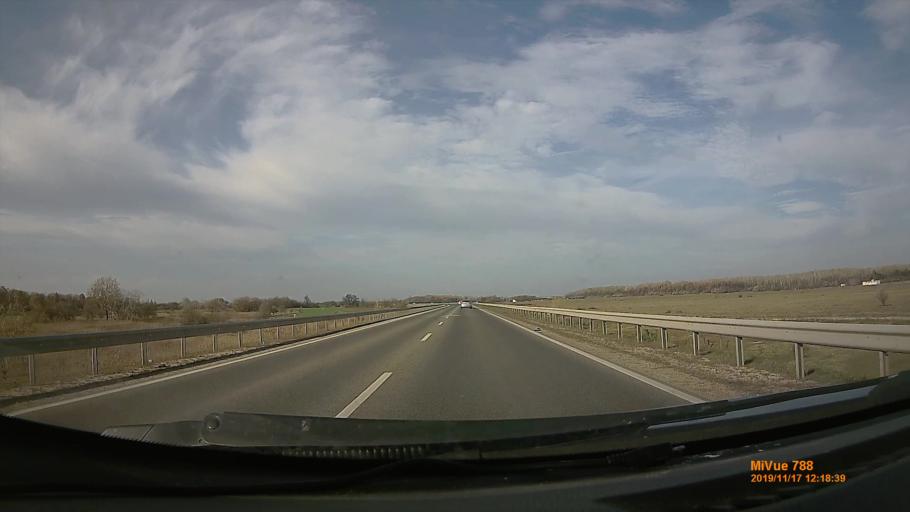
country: HU
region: Bacs-Kiskun
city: Kecskemet
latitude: 46.9214
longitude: 19.7240
